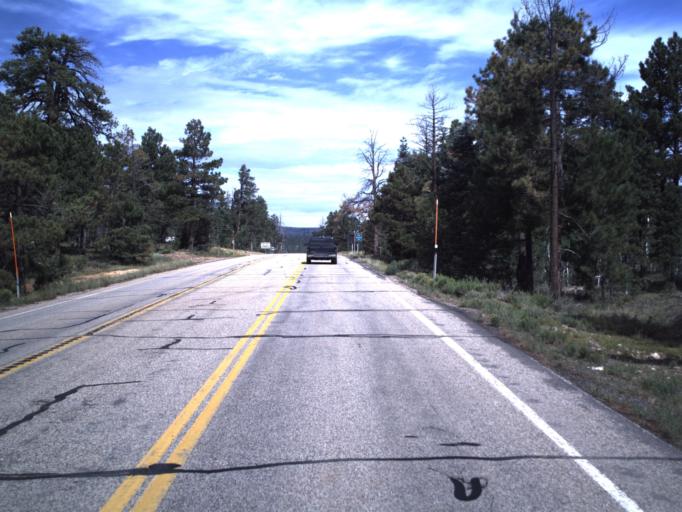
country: US
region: Utah
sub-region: Garfield County
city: Panguitch
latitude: 37.5168
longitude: -112.6445
